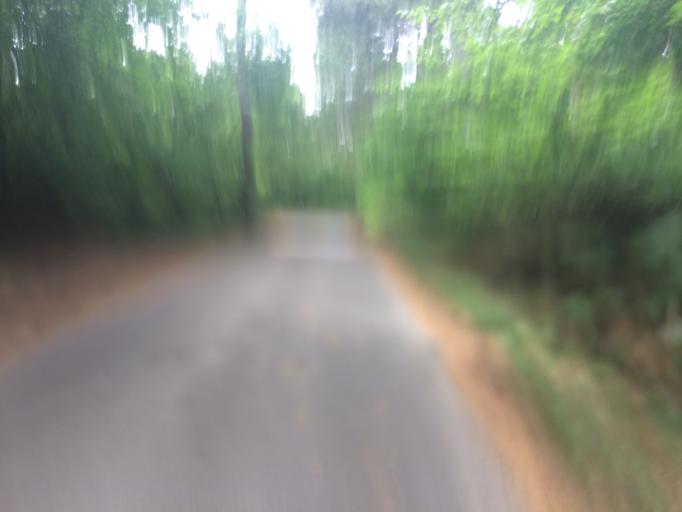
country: DK
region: Capital Region
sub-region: Bornholm Kommune
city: Ronne
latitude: 55.1697
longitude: 14.7199
